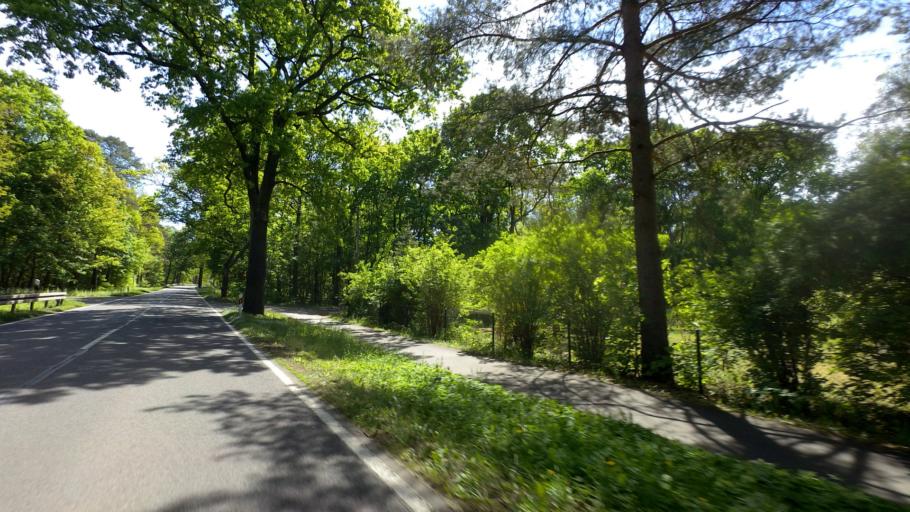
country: DE
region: Brandenburg
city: Luckenwalde
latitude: 52.0696
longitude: 13.1998
